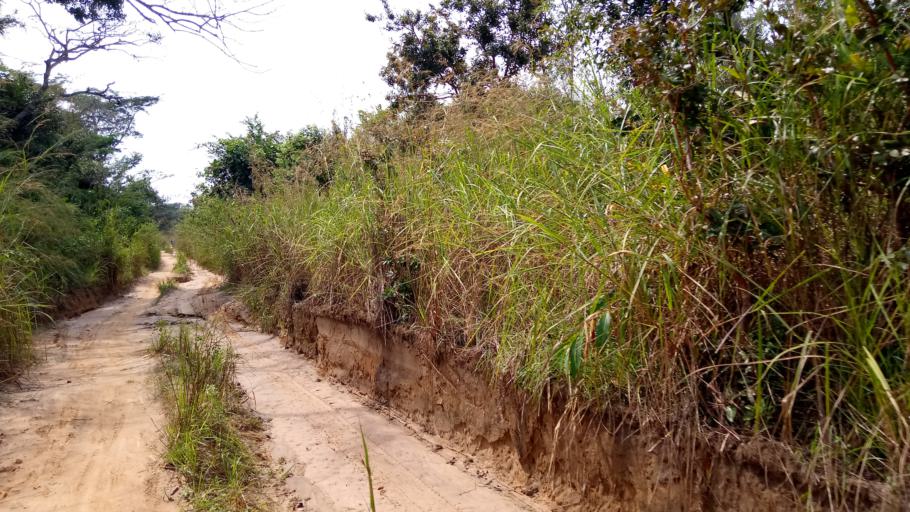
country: CD
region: Bandundu
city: Bandundu
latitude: -4.1503
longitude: 17.4147
